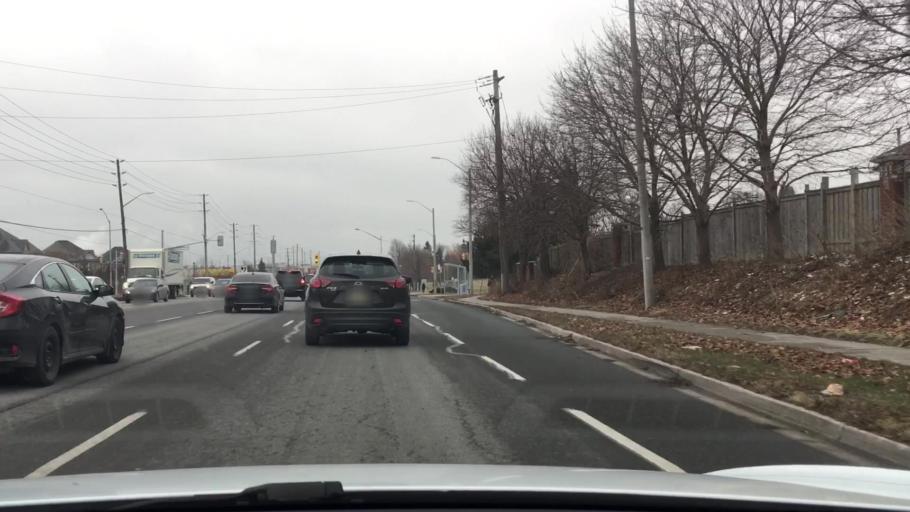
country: CA
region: Ontario
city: Markham
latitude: 43.8416
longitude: -79.2523
